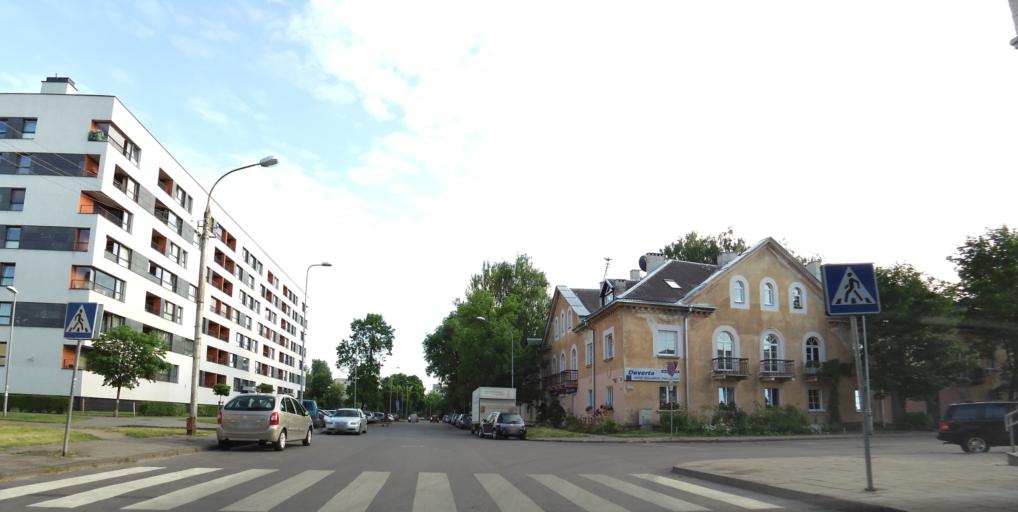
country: LT
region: Vilnius County
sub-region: Vilnius
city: Vilnius
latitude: 54.7095
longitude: 25.2897
